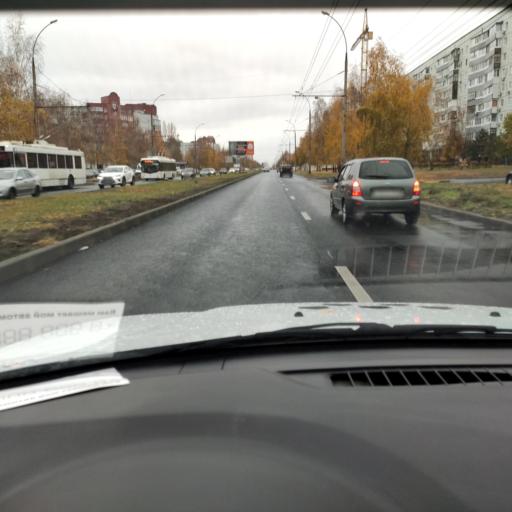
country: RU
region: Samara
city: Tol'yatti
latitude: 53.5265
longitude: 49.3269
